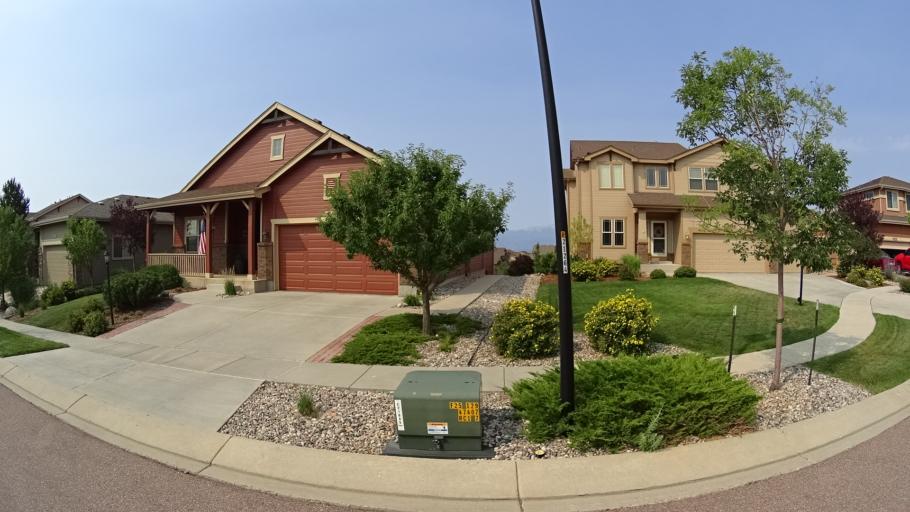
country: US
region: Colorado
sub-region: El Paso County
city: Black Forest
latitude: 38.9701
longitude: -104.7346
